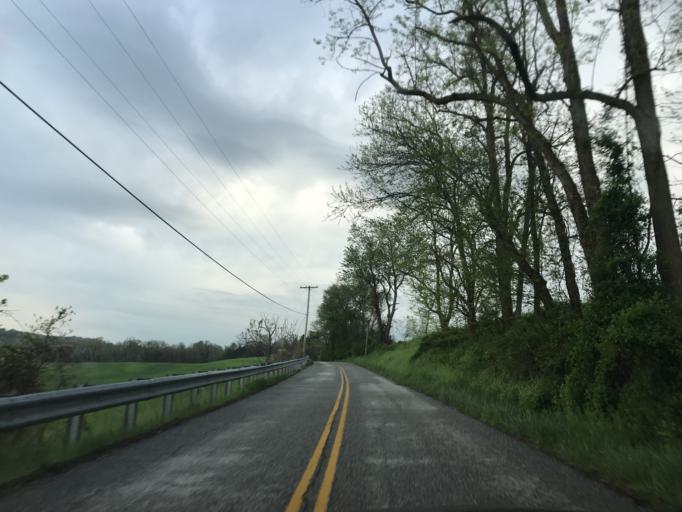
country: US
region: Maryland
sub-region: Harford County
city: Jarrettsville
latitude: 39.6713
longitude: -76.4574
